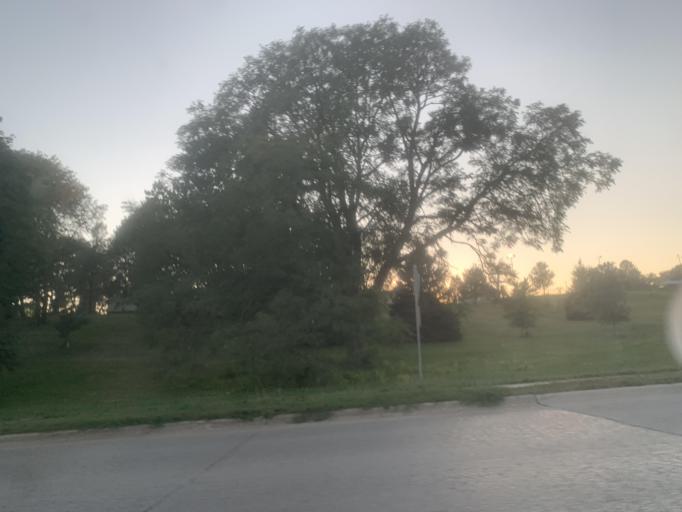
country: US
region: Nebraska
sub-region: Sarpy County
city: La Vista
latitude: 41.2074
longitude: -95.9769
